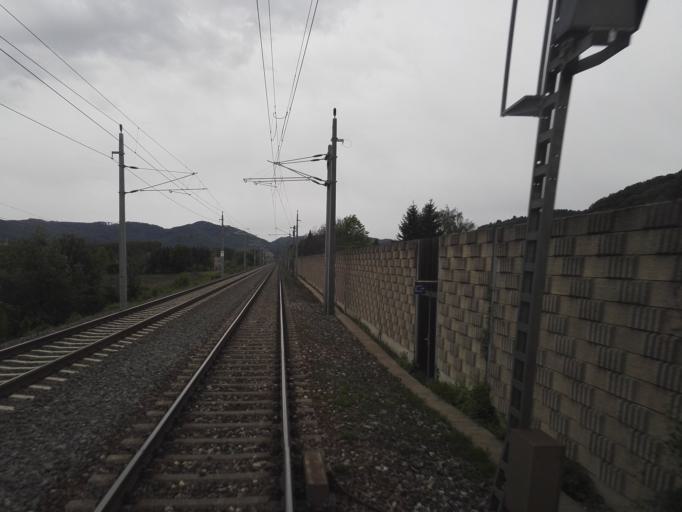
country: AT
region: Styria
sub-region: Politischer Bezirk Graz-Umgebung
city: Gratkorn
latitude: 47.1442
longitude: 15.3244
